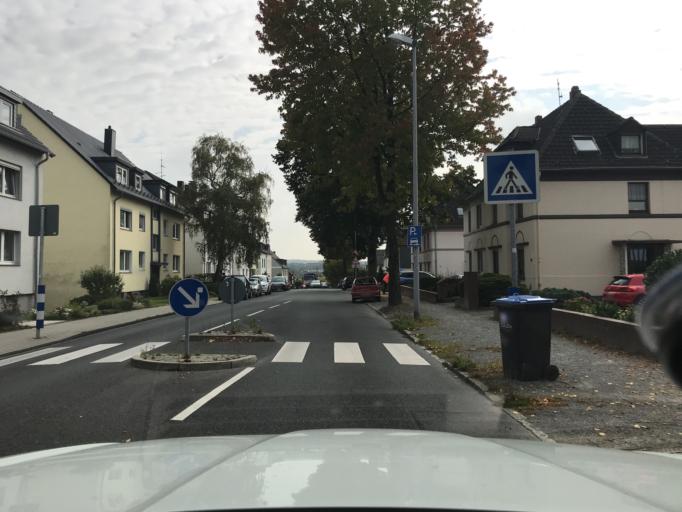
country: DE
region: North Rhine-Westphalia
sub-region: Regierungsbezirk Dusseldorf
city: Muelheim (Ruhr)
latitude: 51.4067
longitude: 6.8543
